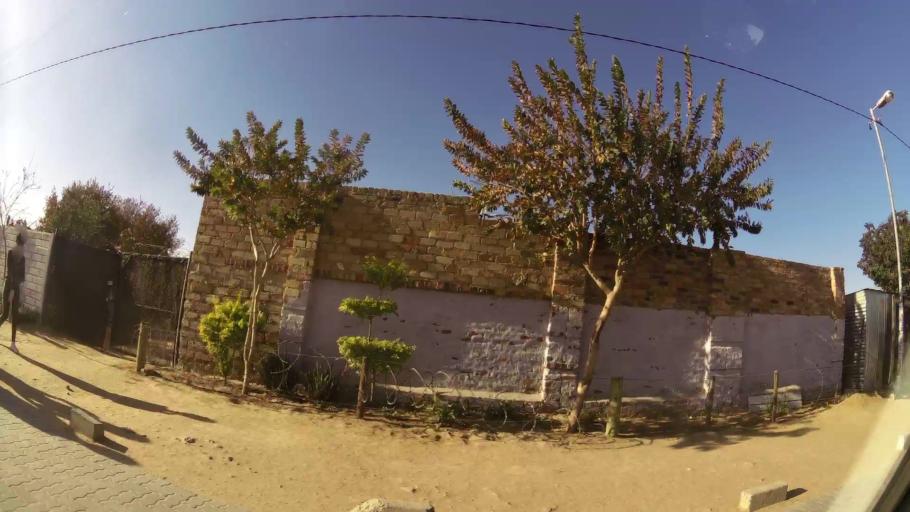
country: ZA
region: Gauteng
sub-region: City of Johannesburg Metropolitan Municipality
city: Diepsloot
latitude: -25.9286
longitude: 28.0025
